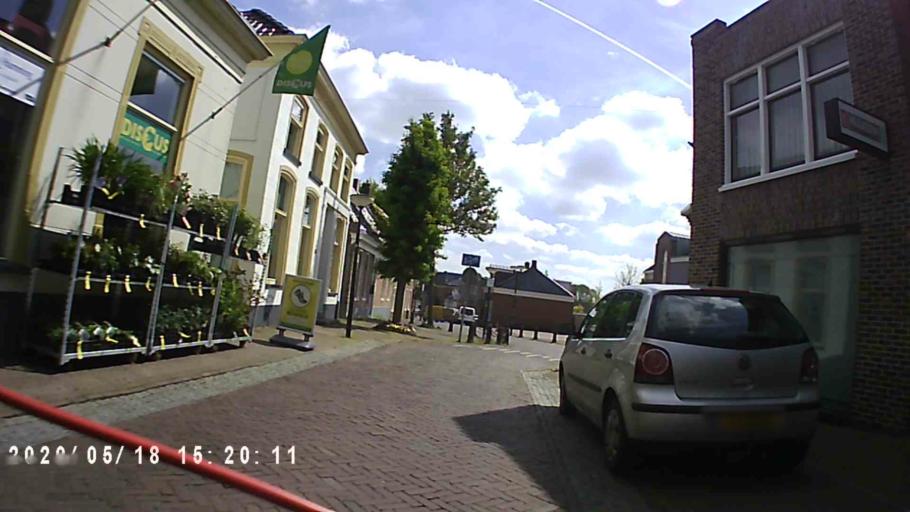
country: NL
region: Groningen
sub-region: Gemeente Winsum
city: Winsum
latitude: 53.3310
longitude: 6.5157
